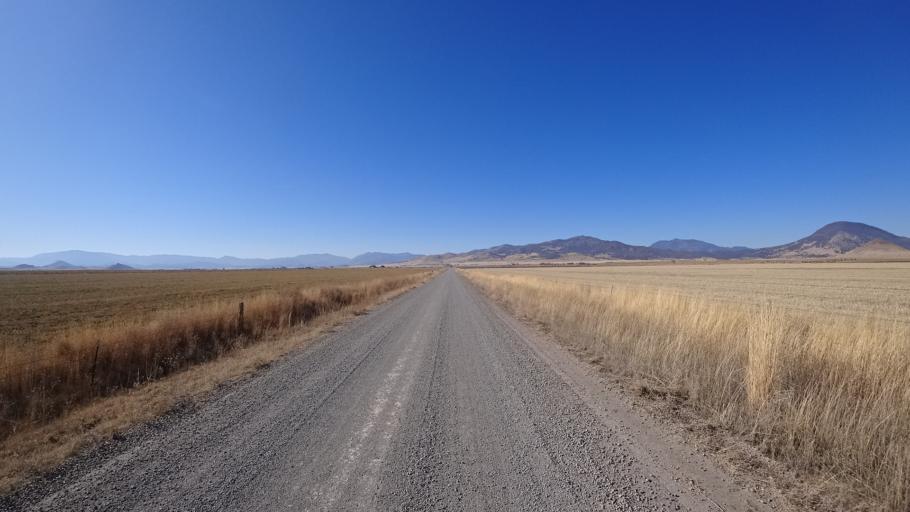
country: US
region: California
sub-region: Siskiyou County
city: Montague
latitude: 41.7865
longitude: -122.4446
